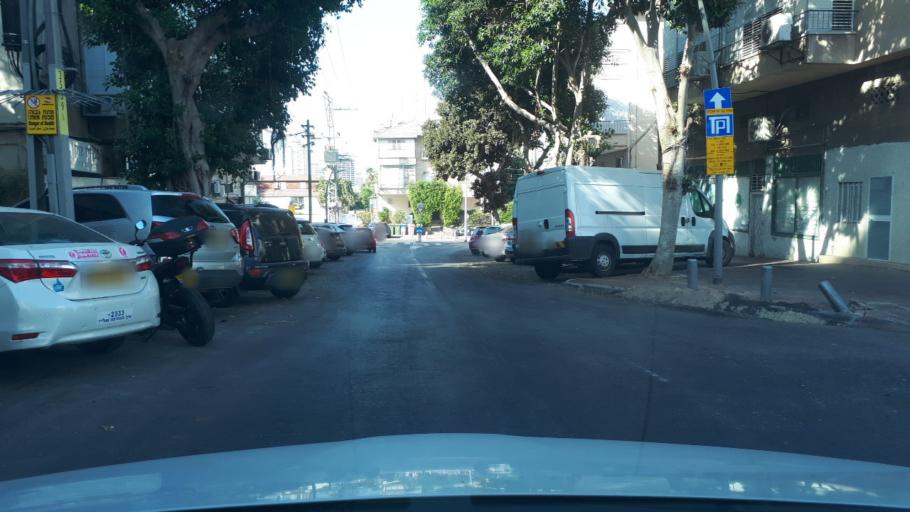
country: IL
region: Tel Aviv
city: Bene Beraq
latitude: 32.0787
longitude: 34.8233
